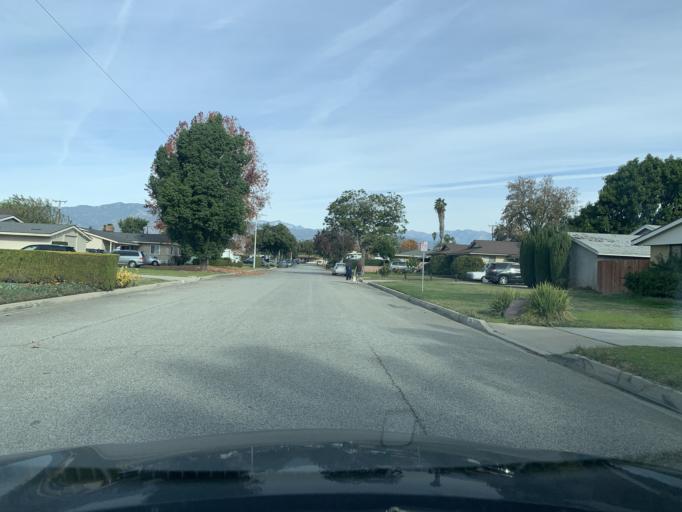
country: US
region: California
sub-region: Los Angeles County
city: West Covina
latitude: 34.0731
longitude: -117.9291
